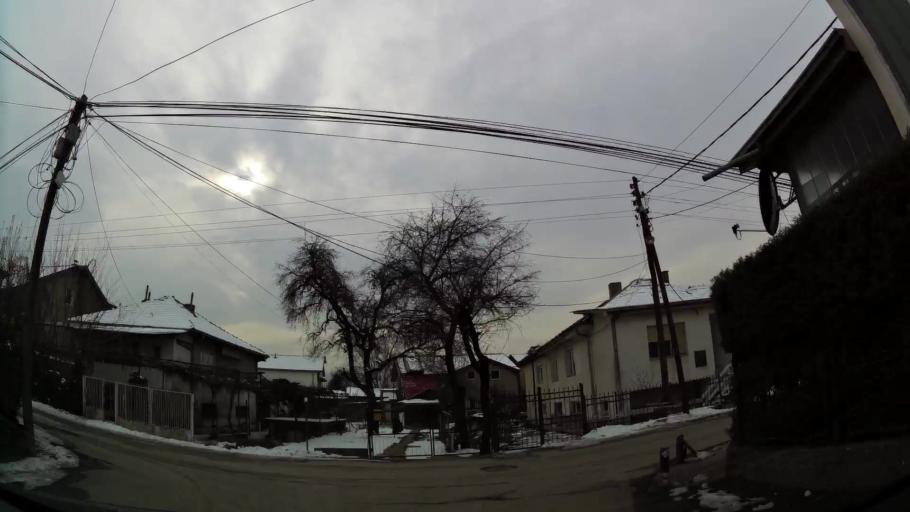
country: MK
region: Butel
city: Butel
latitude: 42.0385
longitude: 21.4504
